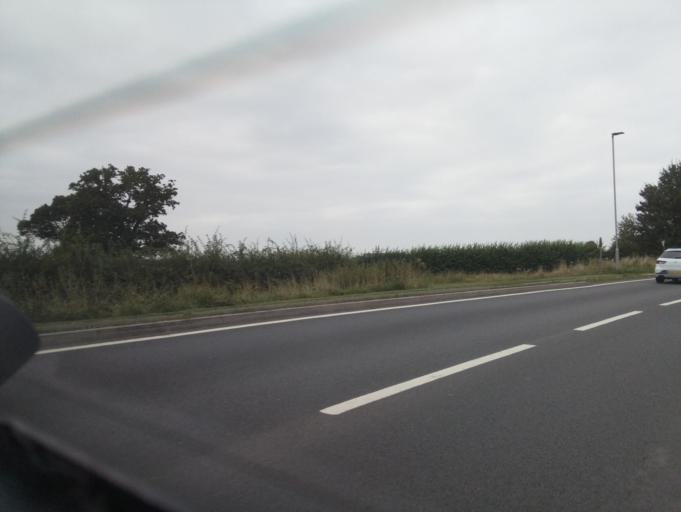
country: GB
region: England
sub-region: Shropshire
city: Shawbury
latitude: 52.7851
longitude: -2.6625
